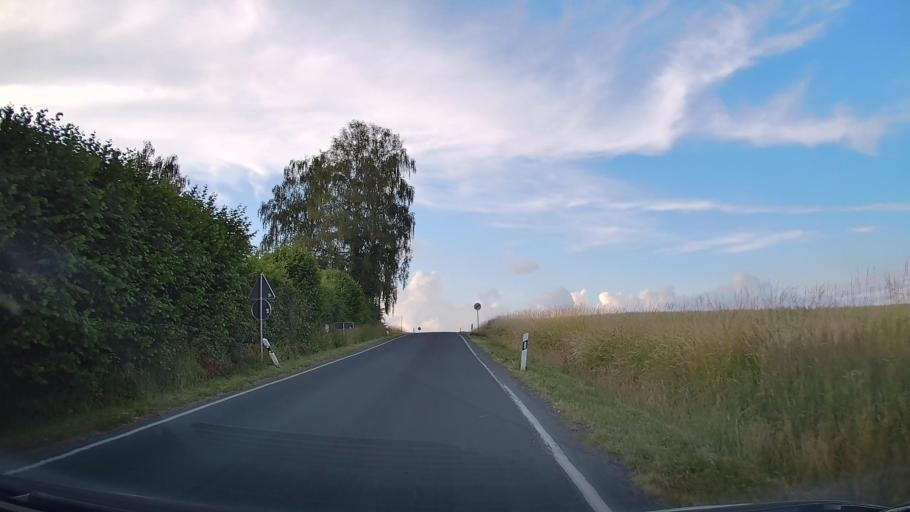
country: DE
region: North Rhine-Westphalia
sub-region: Regierungsbezirk Detmold
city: Barntrup
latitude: 51.9690
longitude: 9.1711
